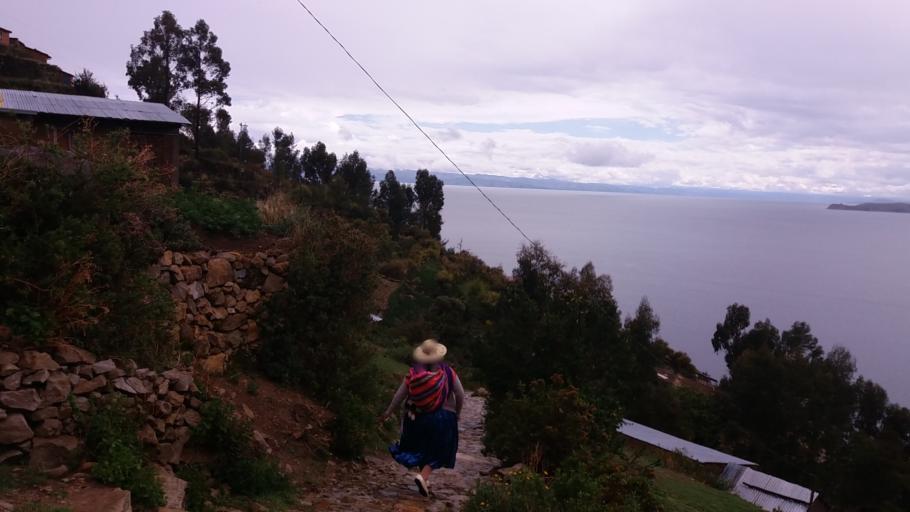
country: BO
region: La Paz
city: Yumani
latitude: -16.0378
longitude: -69.1459
